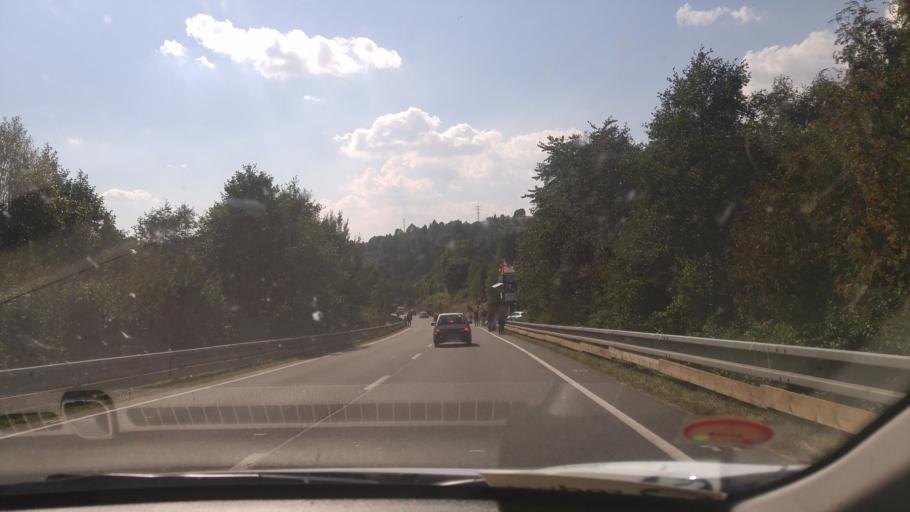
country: CZ
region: Olomoucky
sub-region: Okres Sumperk
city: Stare Mesto
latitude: 50.1567
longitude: 17.0132
